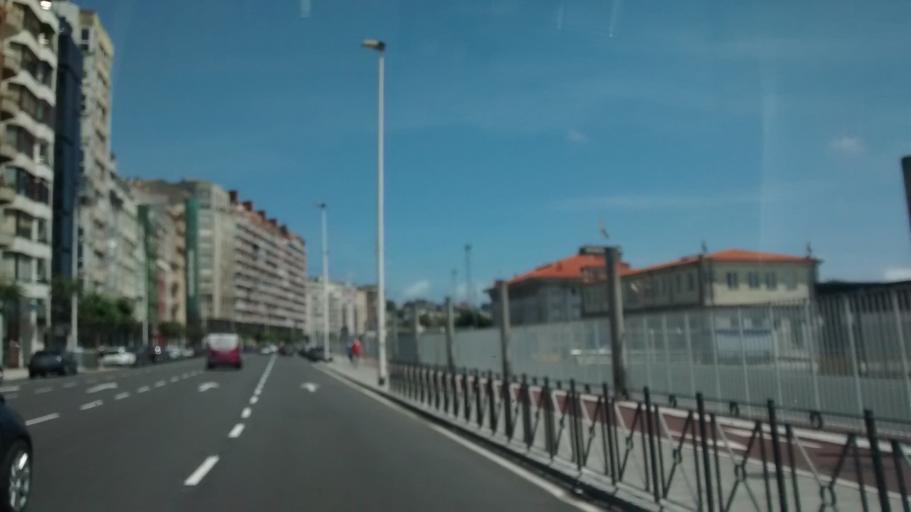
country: ES
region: Cantabria
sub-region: Provincia de Cantabria
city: Santander
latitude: 43.4558
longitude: -3.8109
